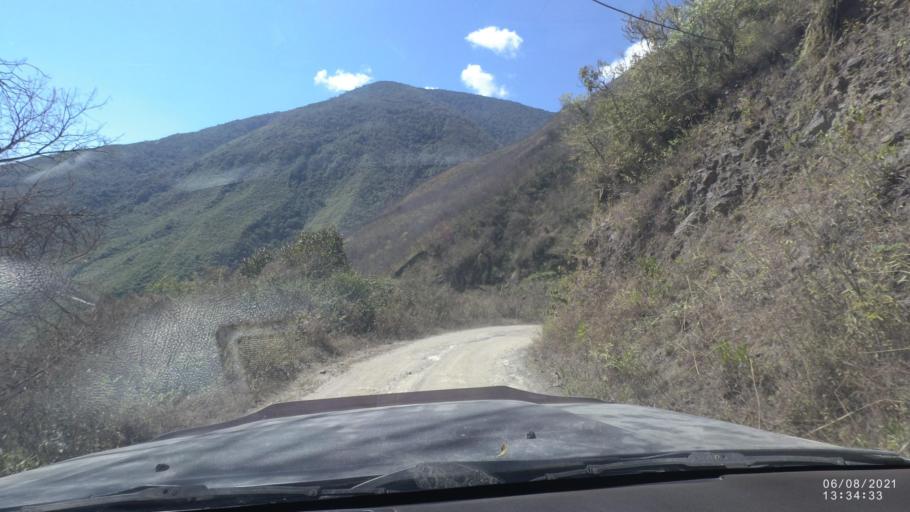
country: BO
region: La Paz
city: Quime
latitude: -16.6947
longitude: -66.7227
